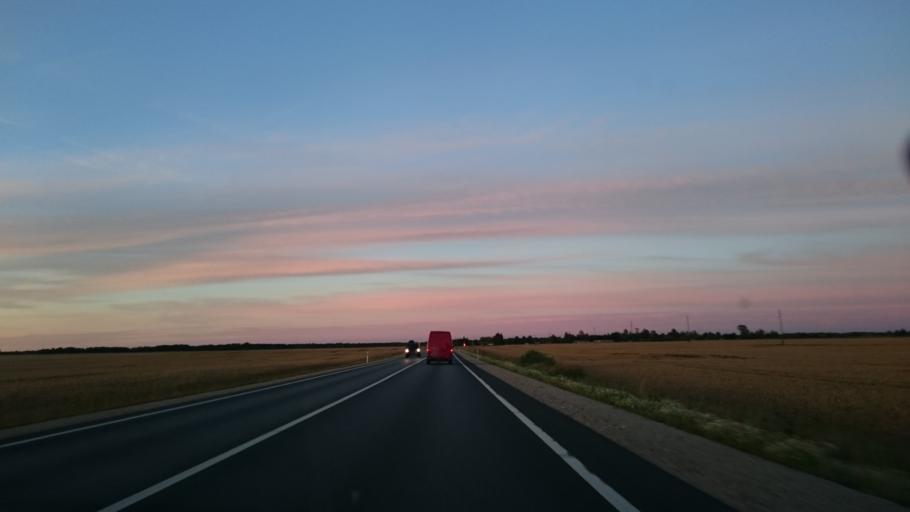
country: LV
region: Dobeles Rajons
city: Dobele
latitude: 56.7379
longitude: 23.2334
